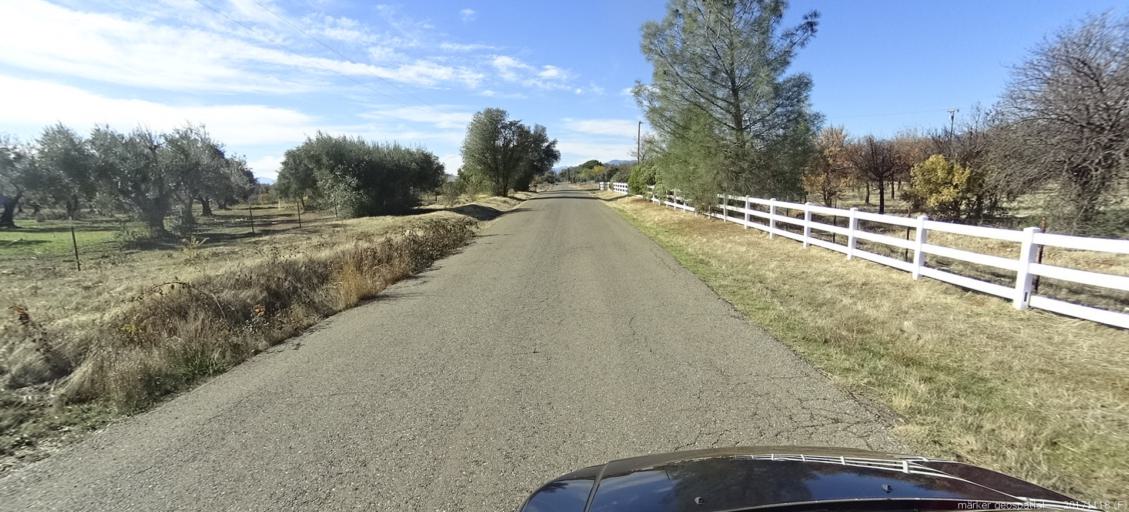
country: US
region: California
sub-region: Shasta County
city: Redding
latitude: 40.4562
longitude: -122.4449
